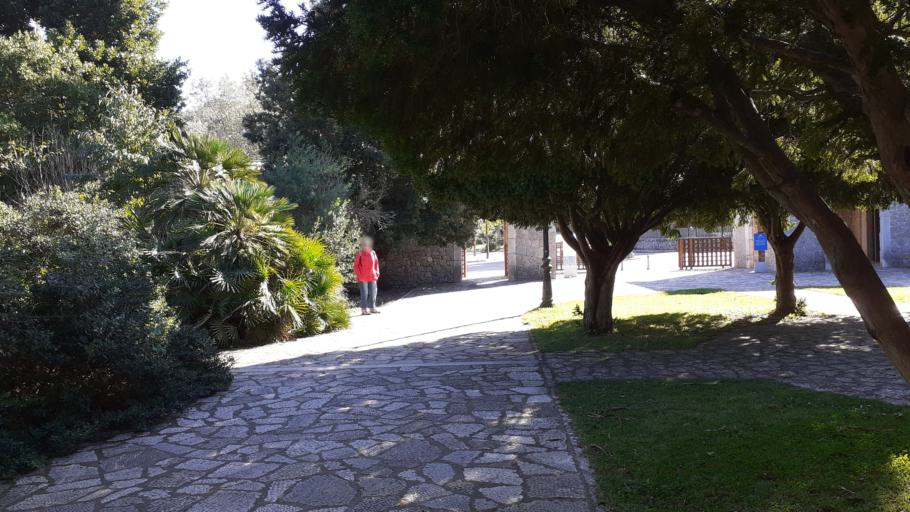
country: ES
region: Balearic Islands
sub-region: Illes Balears
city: Escorca
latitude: 39.8225
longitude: 2.8839
